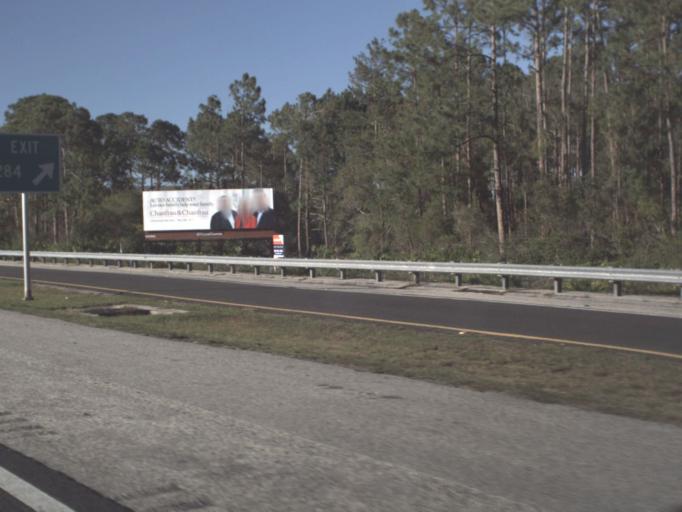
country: US
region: Florida
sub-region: Flagler County
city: Flagler Beach
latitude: 29.4717
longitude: -81.1820
